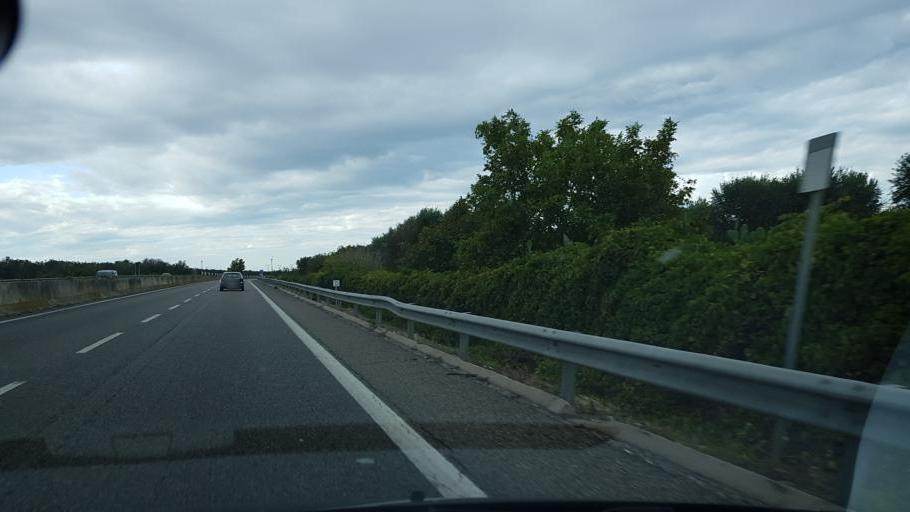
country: IT
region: Apulia
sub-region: Provincia di Brindisi
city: San Pietro Vernotico
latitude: 40.5387
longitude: 18.0044
